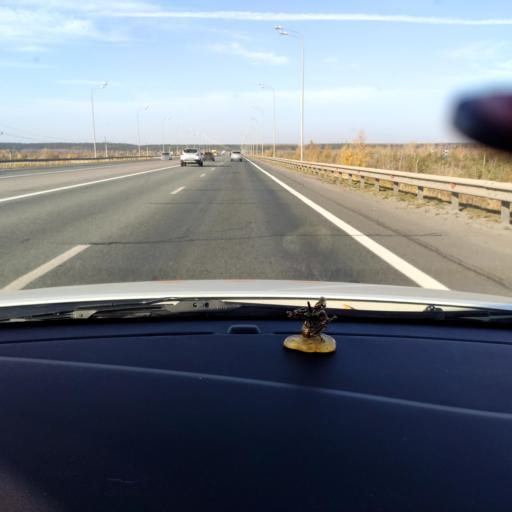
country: RU
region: Tatarstan
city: Osinovo
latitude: 55.8023
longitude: 48.8416
